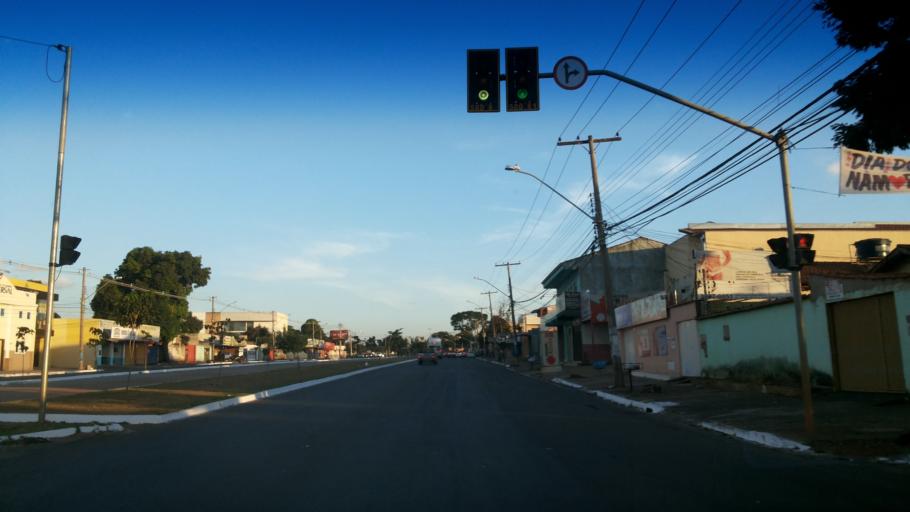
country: BR
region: Goias
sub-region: Goiania
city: Goiania
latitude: -16.6355
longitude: -49.2728
